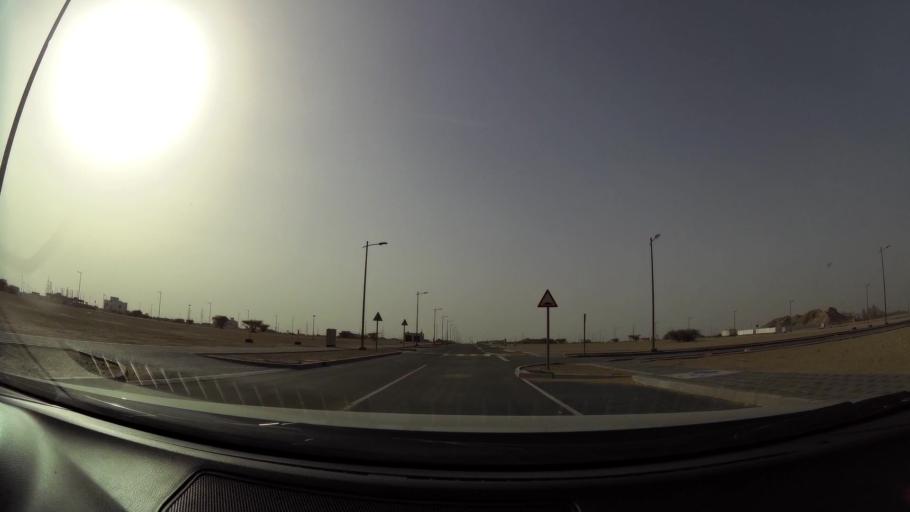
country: AE
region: Abu Dhabi
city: Al Ain
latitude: 24.1186
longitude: 55.7244
